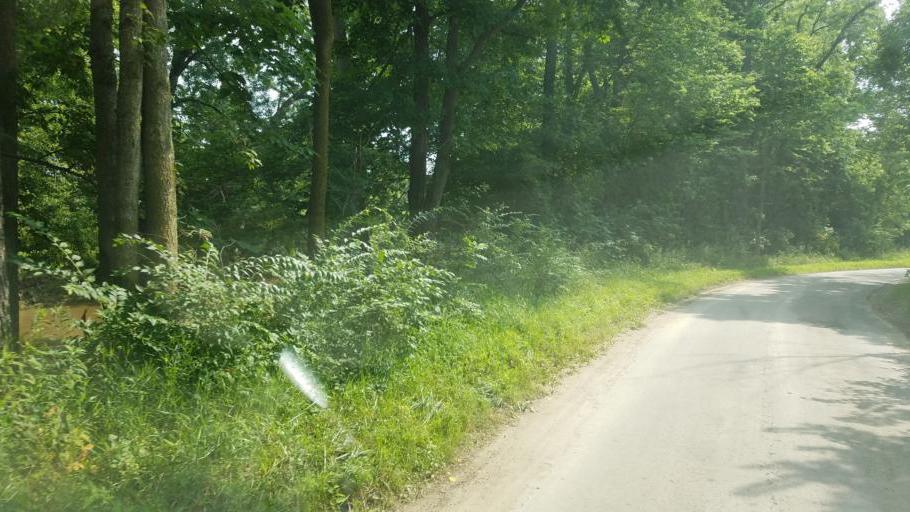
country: US
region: Ohio
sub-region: Hardin County
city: Kenton
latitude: 40.6201
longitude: -83.5280
